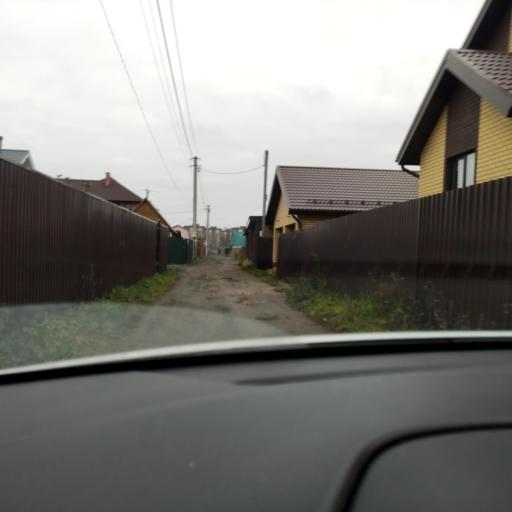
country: RU
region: Tatarstan
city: Stolbishchi
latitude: 55.6930
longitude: 49.2140
